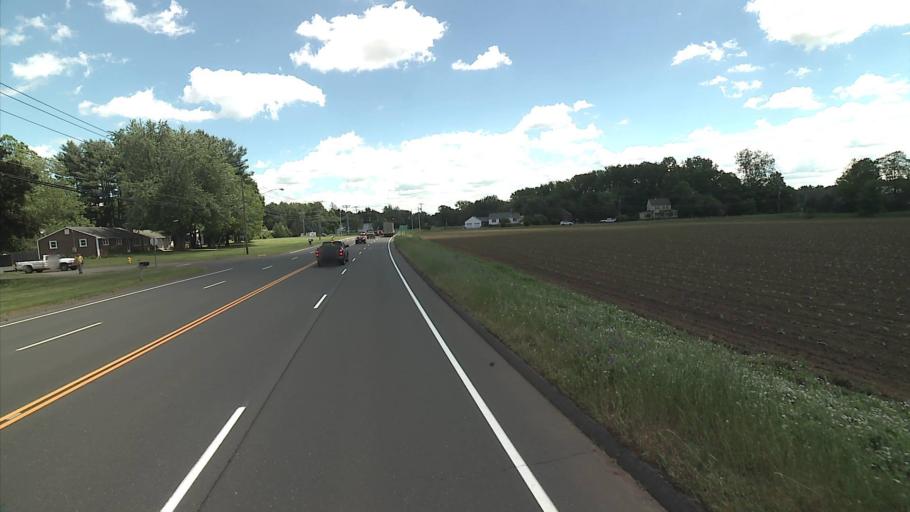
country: US
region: Connecticut
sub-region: Hartford County
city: Sherwood Manor
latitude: 42.0093
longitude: -72.5447
